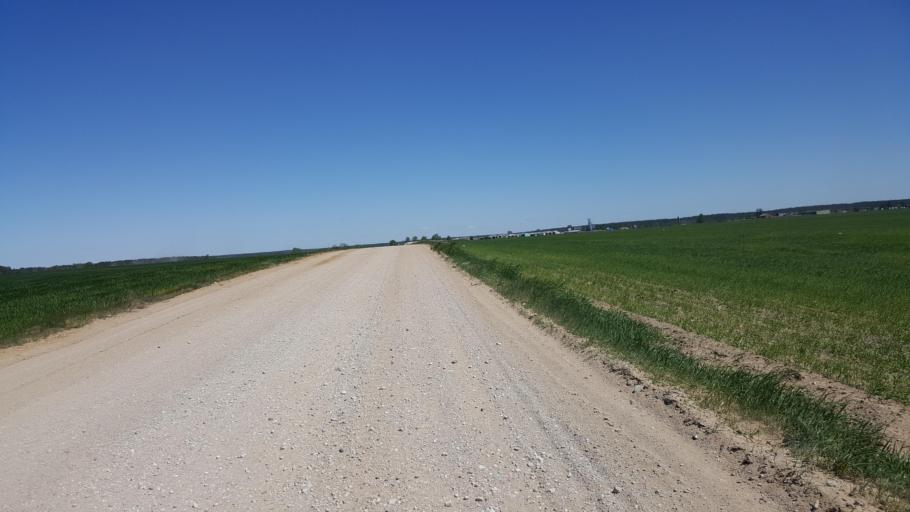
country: BY
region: Brest
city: Kamyanyuki
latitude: 52.4901
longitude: 23.7483
